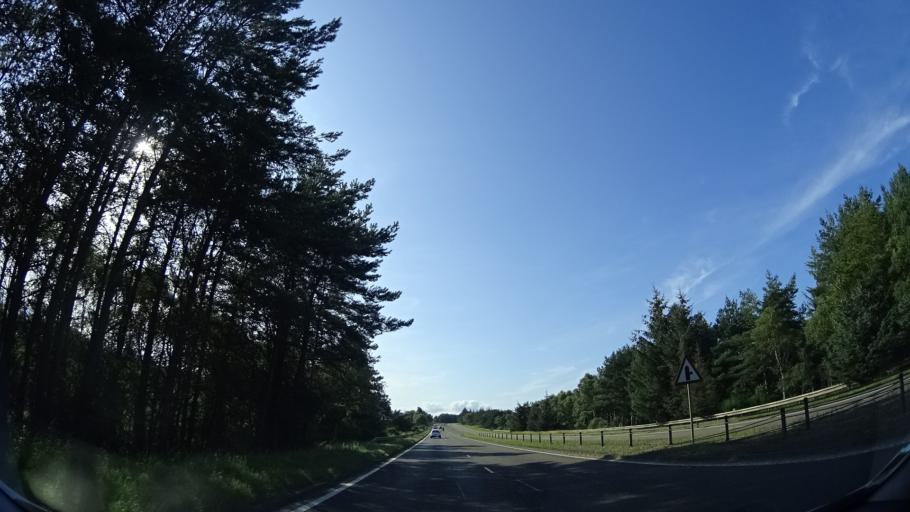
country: GB
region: Scotland
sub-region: Highland
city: Inverness
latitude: 57.5207
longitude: -4.3091
